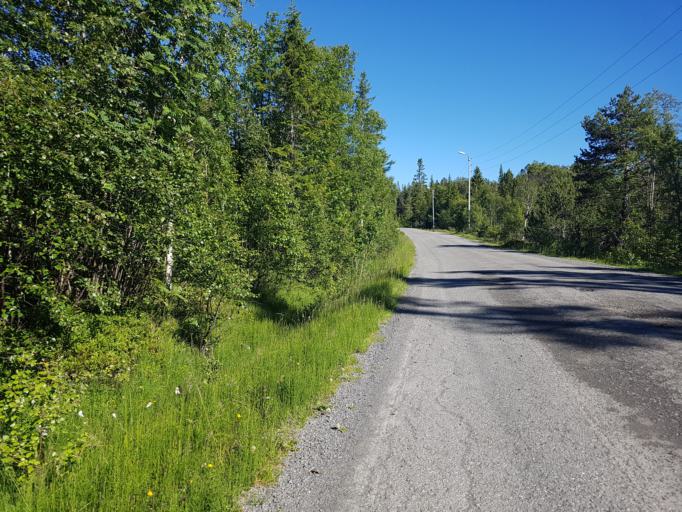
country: NO
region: Sor-Trondelag
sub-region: Trondheim
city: Trondheim
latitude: 63.4286
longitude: 10.2811
